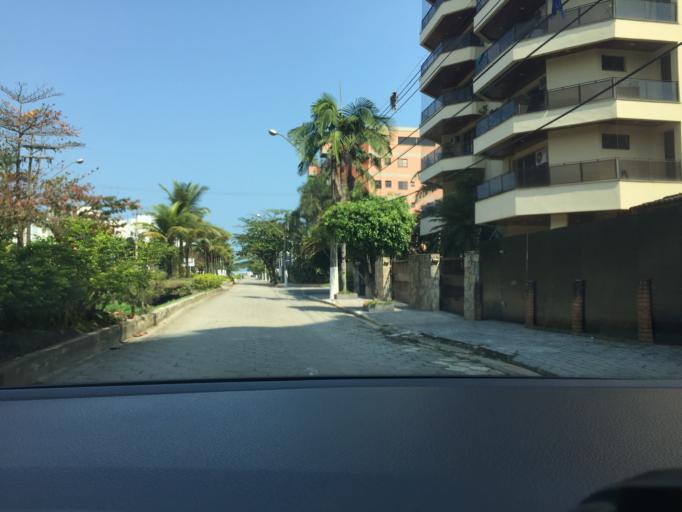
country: BR
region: Sao Paulo
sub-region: Guaruja
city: Guaruja
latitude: -23.9810
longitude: -46.2218
